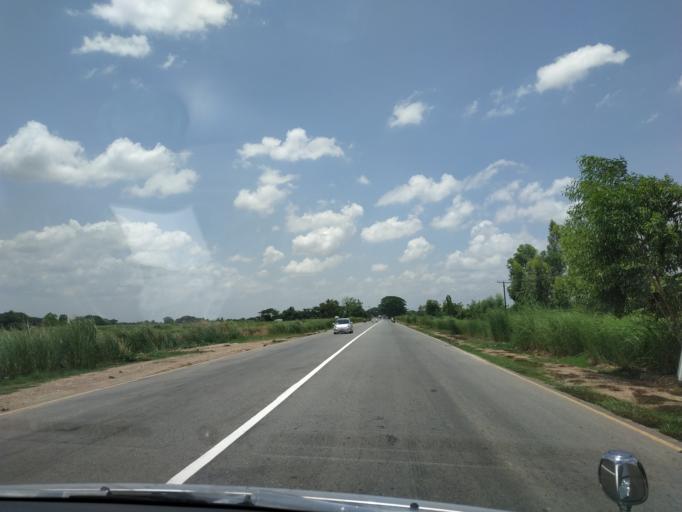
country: MM
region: Bago
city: Thanatpin
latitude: 17.4608
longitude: 96.6509
